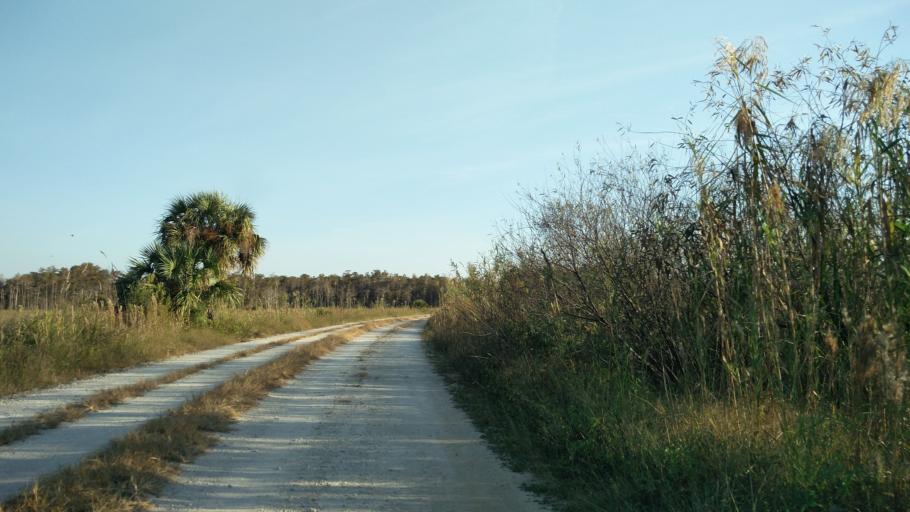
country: US
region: Florida
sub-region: Collier County
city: Lely Resort
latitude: 25.9786
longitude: -81.3708
